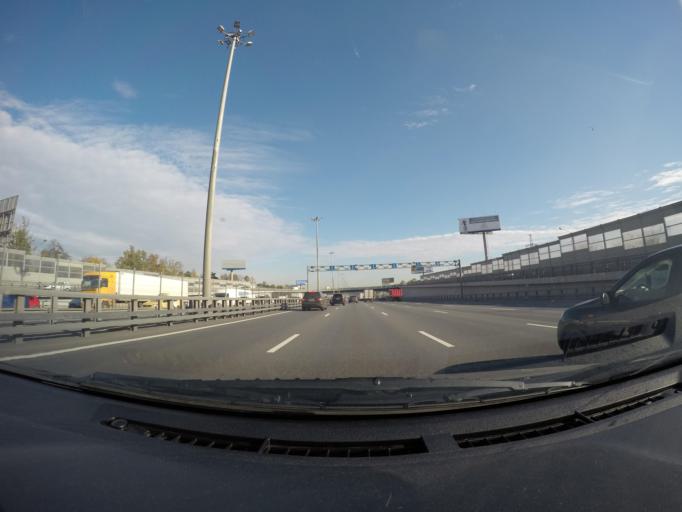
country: RU
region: Moskovskaya
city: Druzhba
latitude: 55.8946
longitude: 37.7477
